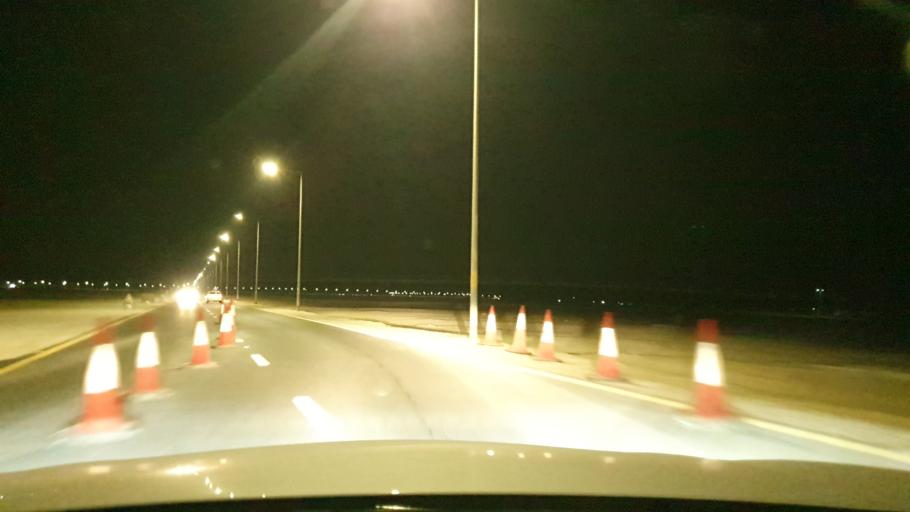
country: BH
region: Muharraq
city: Al Muharraq
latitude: 26.2809
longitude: 50.5894
